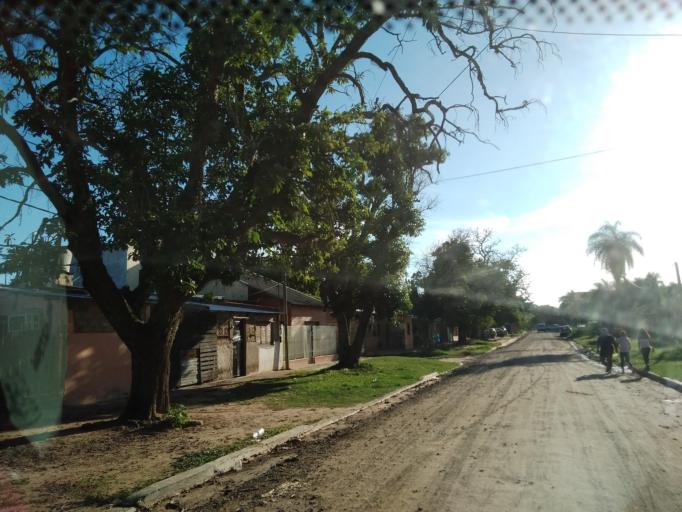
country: AR
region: Corrientes
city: Corrientes
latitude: -27.5067
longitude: -58.7944
